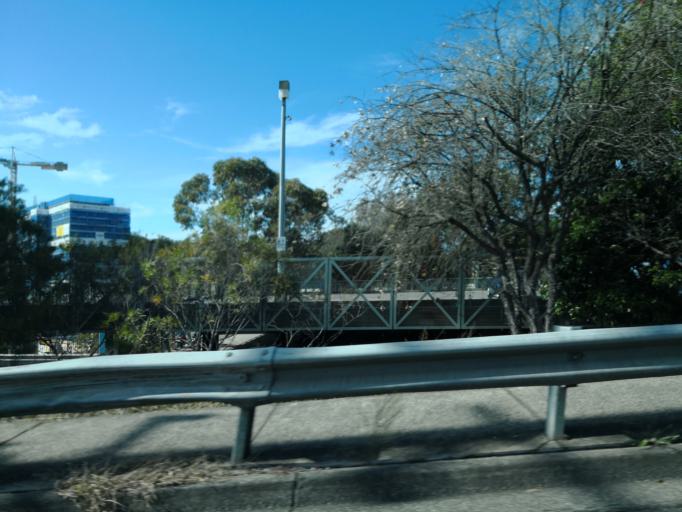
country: AU
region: New South Wales
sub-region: Gosford Shire
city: Gosford
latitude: -33.4247
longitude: 151.3407
